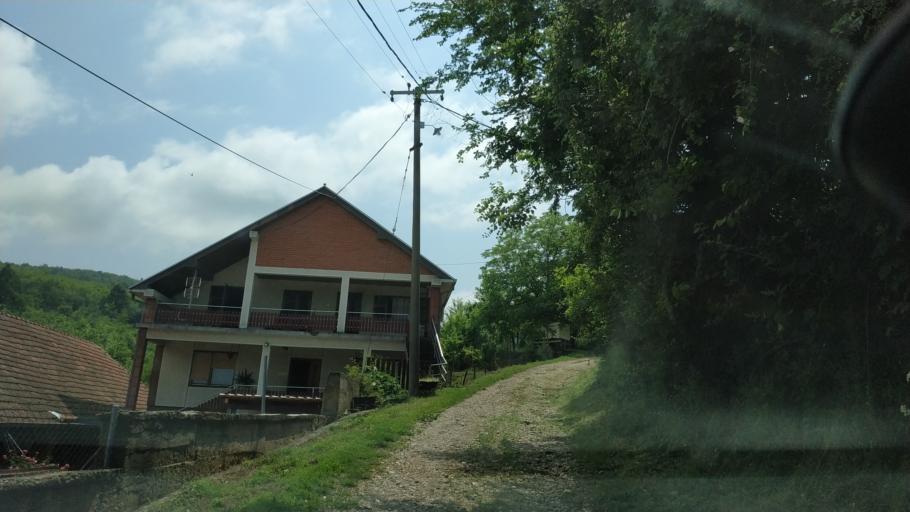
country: RS
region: Central Serbia
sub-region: Nisavski Okrug
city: Merosina
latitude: 43.4123
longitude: 21.7168
